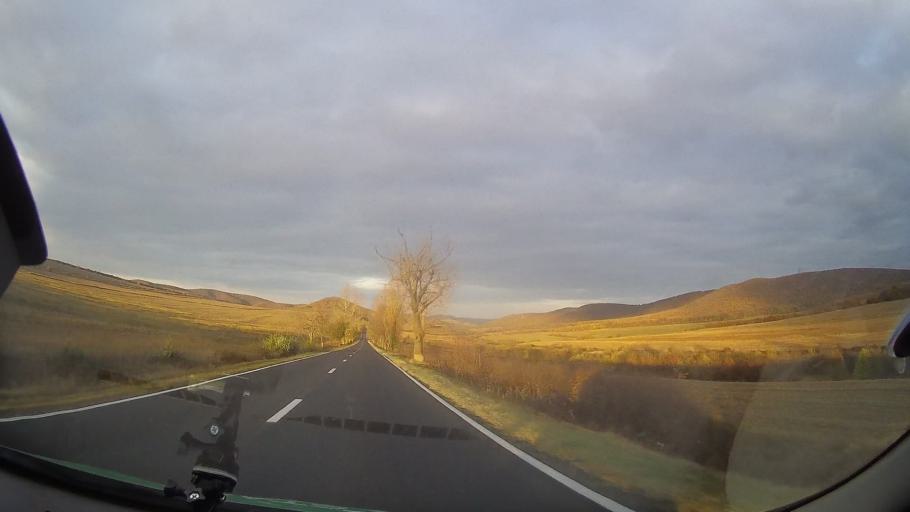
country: RO
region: Tulcea
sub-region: Comuna Ciucurova
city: Ciucurova
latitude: 44.9336
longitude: 28.4874
